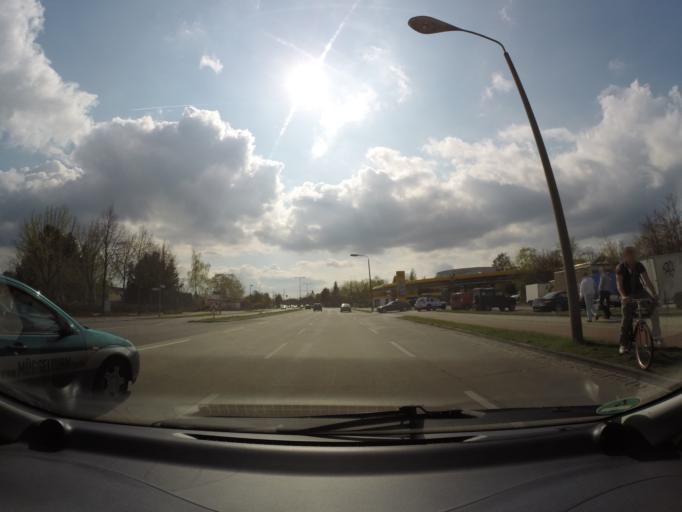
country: DE
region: Berlin
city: Marzahn
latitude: 52.5372
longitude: 13.5795
